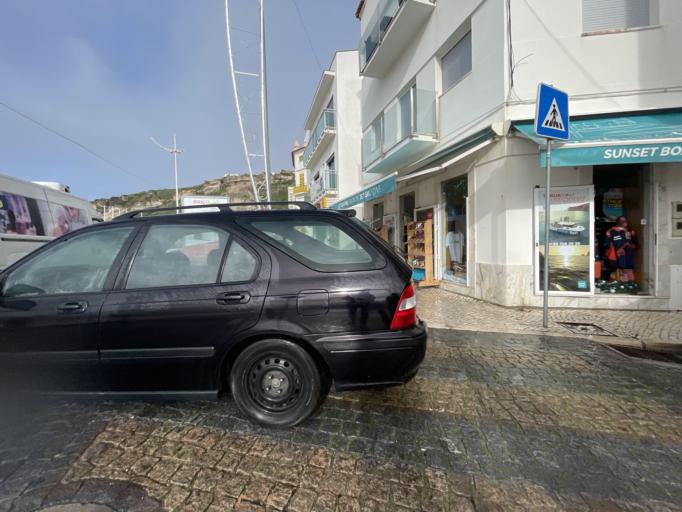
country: PT
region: Leiria
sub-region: Nazare
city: Nazare
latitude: 39.6011
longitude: -9.0736
